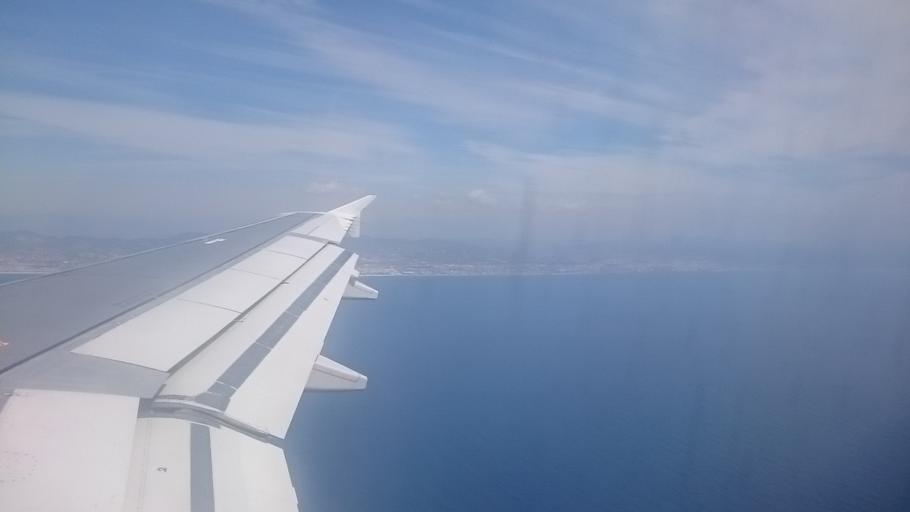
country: ES
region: Catalonia
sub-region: Provincia de Barcelona
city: Premia de Mar
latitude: 41.4053
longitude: 2.3962
